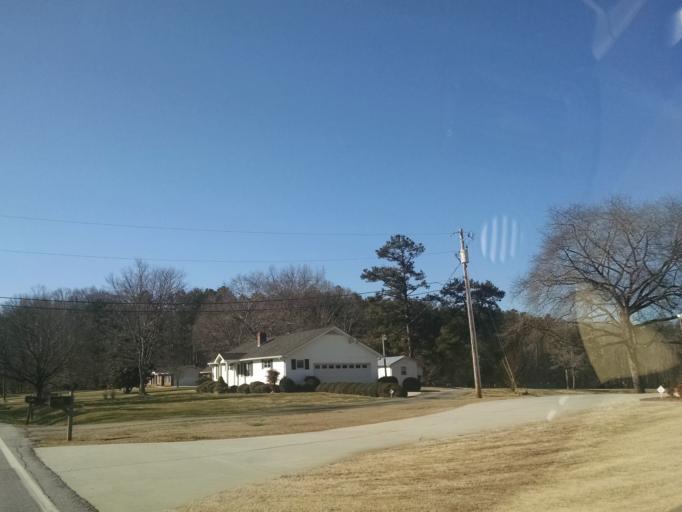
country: US
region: Georgia
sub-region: Gwinnett County
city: Sugar Hill
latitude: 34.1018
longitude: -84.0627
